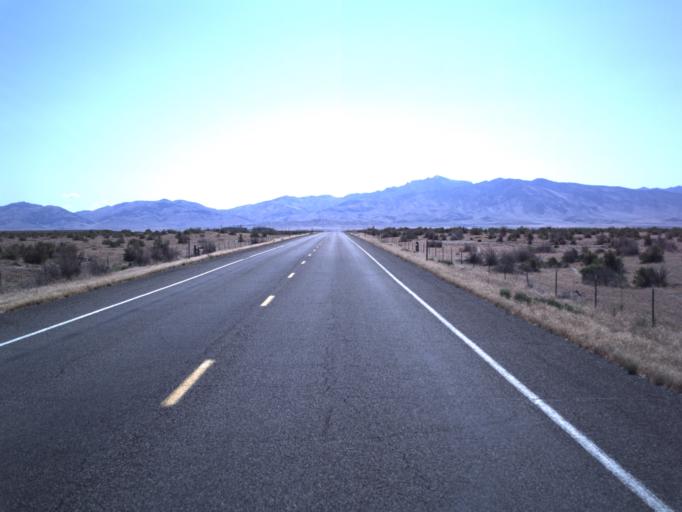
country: US
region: Utah
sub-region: Millard County
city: Delta
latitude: 39.4719
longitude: -112.4686
